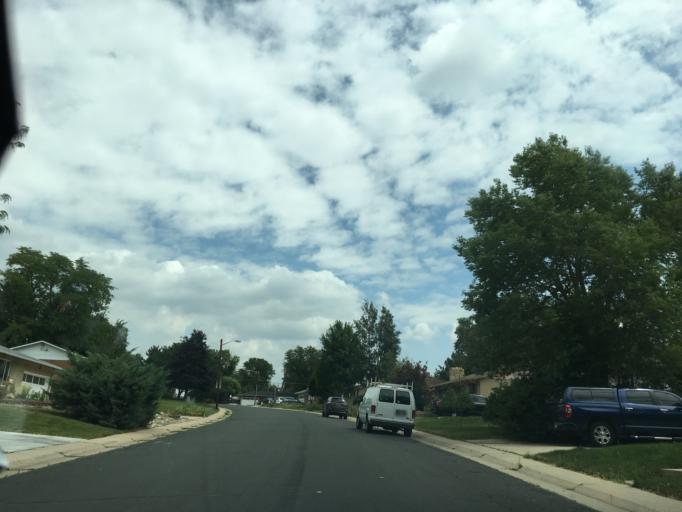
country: US
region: Colorado
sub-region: Arapahoe County
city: Sheridan
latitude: 39.6649
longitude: -105.0394
